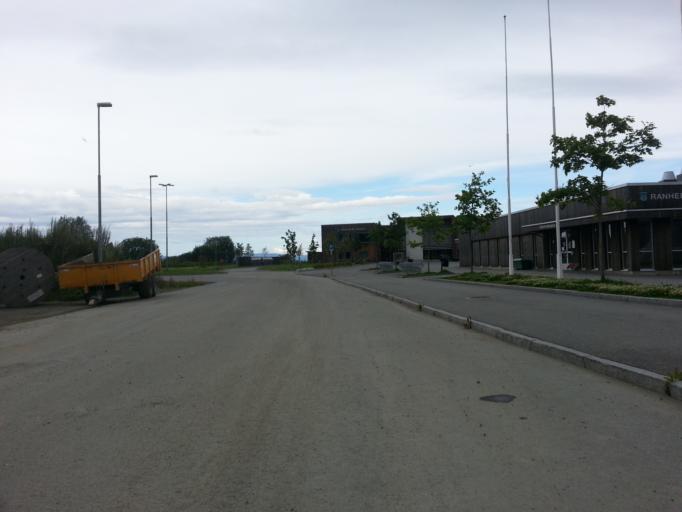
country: NO
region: Sor-Trondelag
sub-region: Trondheim
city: Trondheim
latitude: 63.4286
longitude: 10.5218
